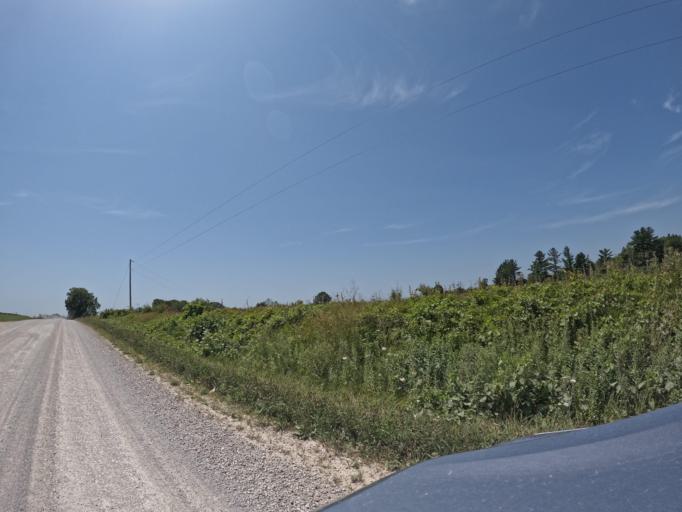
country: US
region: Iowa
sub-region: Henry County
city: Mount Pleasant
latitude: 40.9354
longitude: -91.5831
